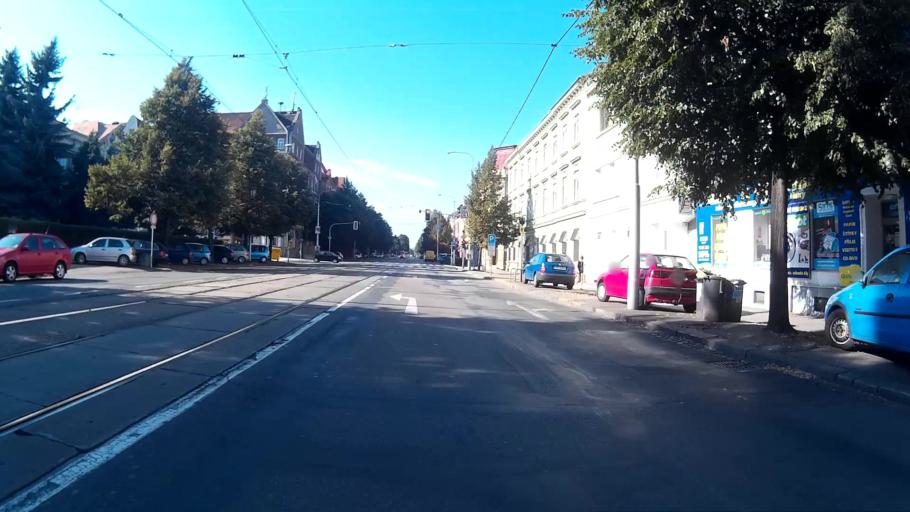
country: CZ
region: South Moravian
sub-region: Mesto Brno
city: Brno
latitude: 49.2149
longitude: 16.6003
